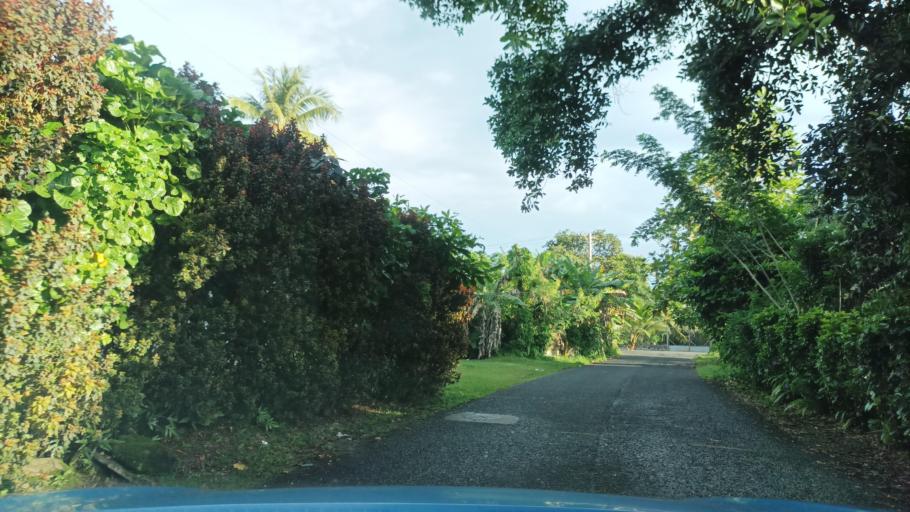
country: FM
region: Pohnpei
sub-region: Kolonia Municipality
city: Kolonia
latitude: 6.9686
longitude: 158.2073
